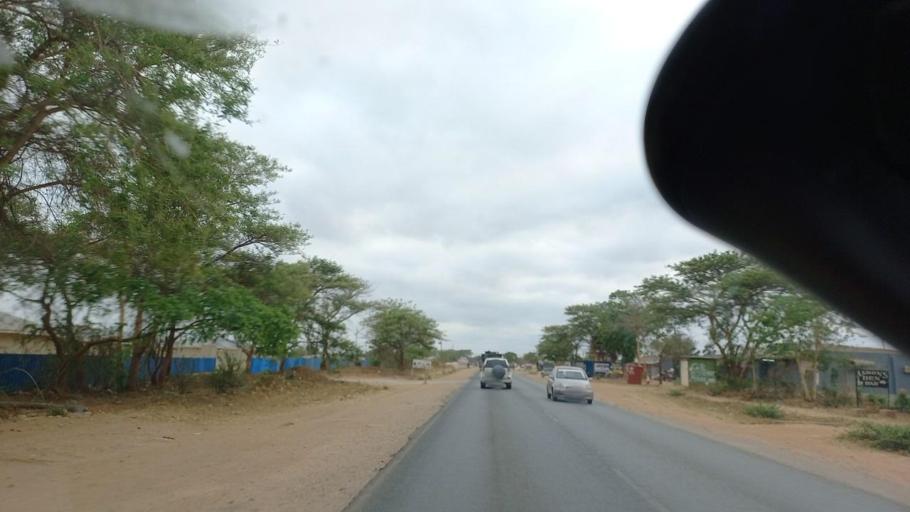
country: ZM
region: Lusaka
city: Chongwe
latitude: -15.3367
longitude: 28.6694
